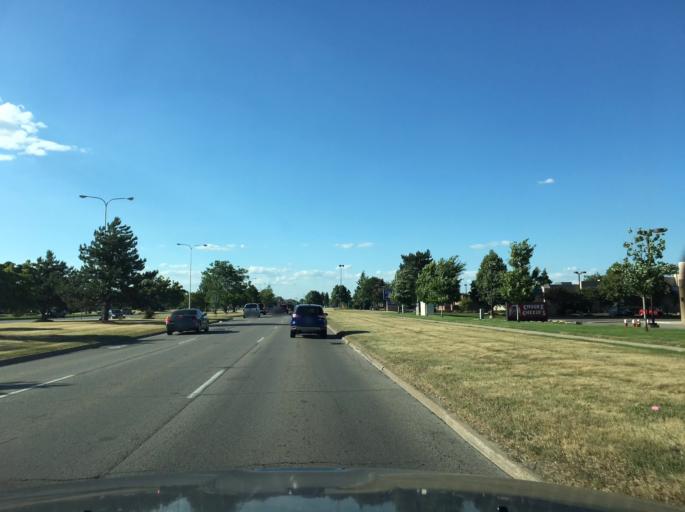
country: US
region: Michigan
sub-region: Macomb County
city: Utica
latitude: 42.6222
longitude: -82.9925
